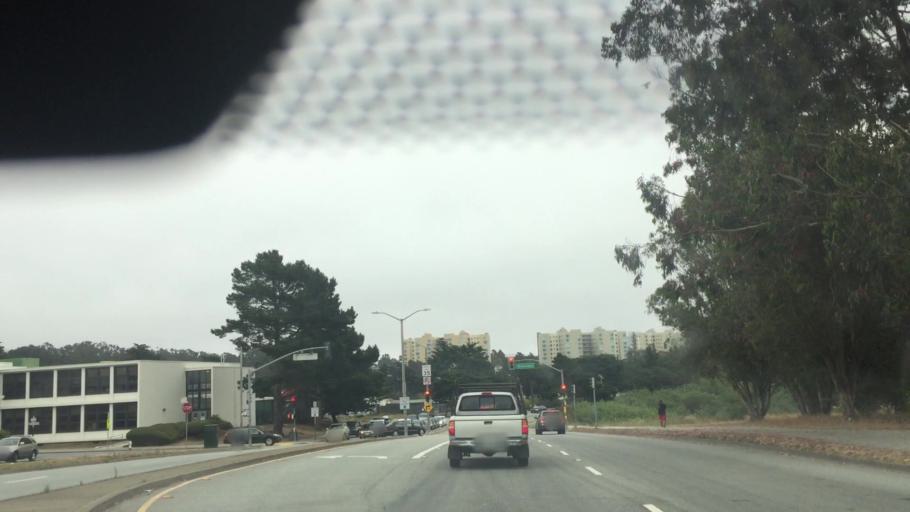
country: US
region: California
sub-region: San Mateo County
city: Daly City
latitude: 37.7298
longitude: -122.4875
